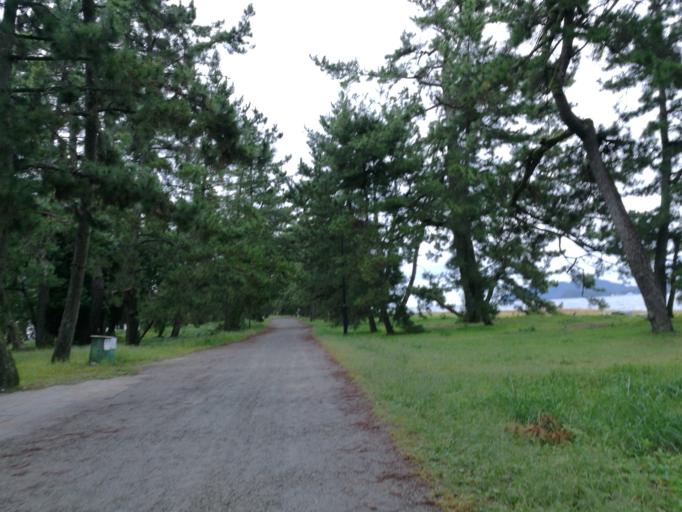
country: JP
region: Kyoto
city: Miyazu
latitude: 35.5751
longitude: 135.1960
